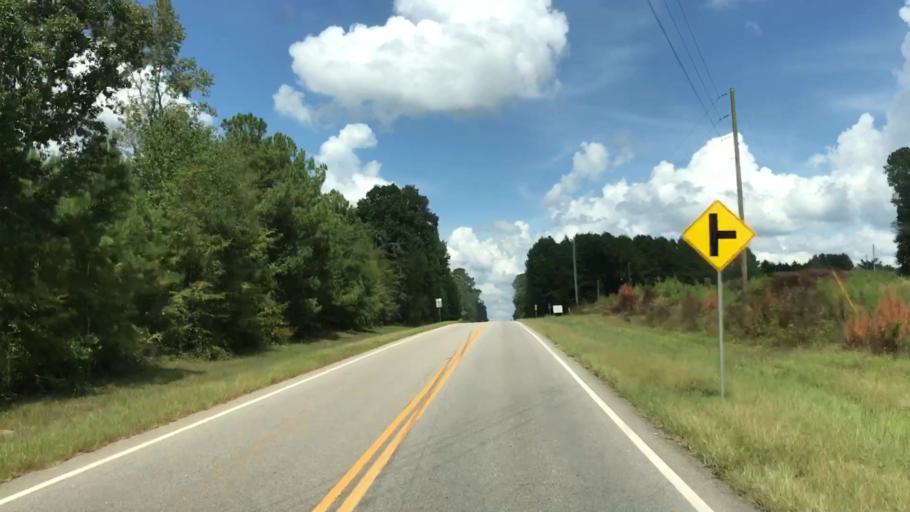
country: US
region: Georgia
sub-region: Greene County
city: Greensboro
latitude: 33.6167
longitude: -83.2105
